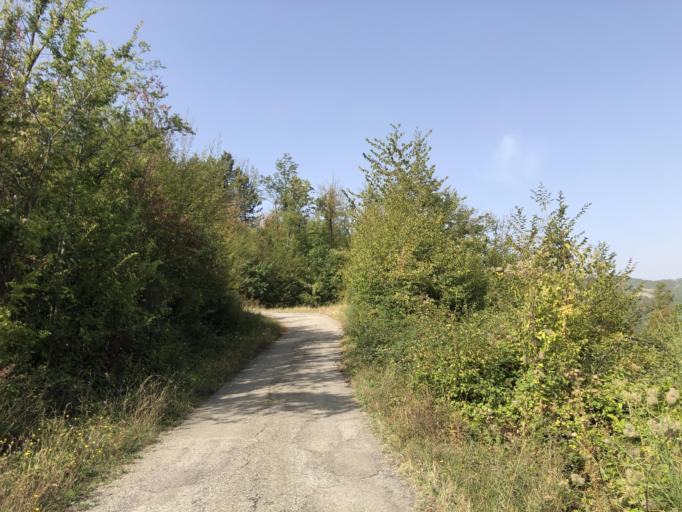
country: IT
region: Emilia-Romagna
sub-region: Forli-Cesena
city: Portico e San Benedetto
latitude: 44.0180
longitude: 11.7859
